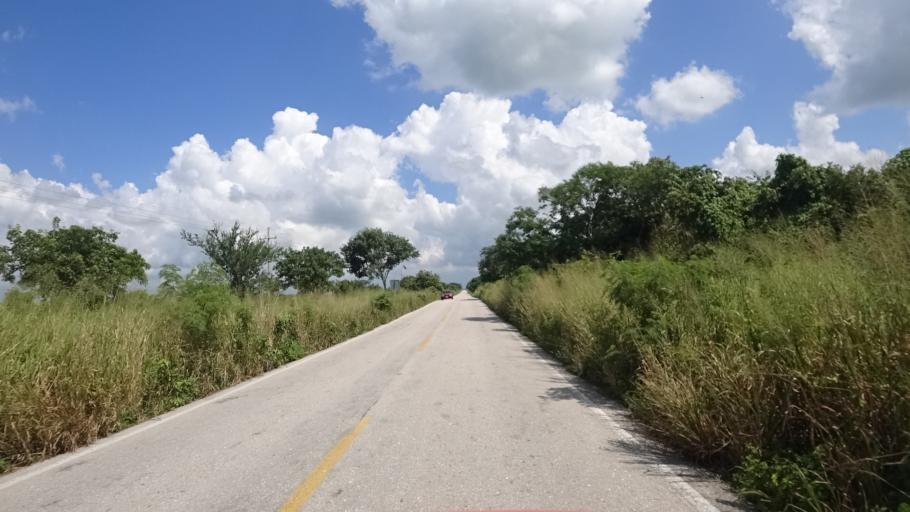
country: MX
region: Yucatan
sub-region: Panaba
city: Loche
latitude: 21.4574
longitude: -88.1322
